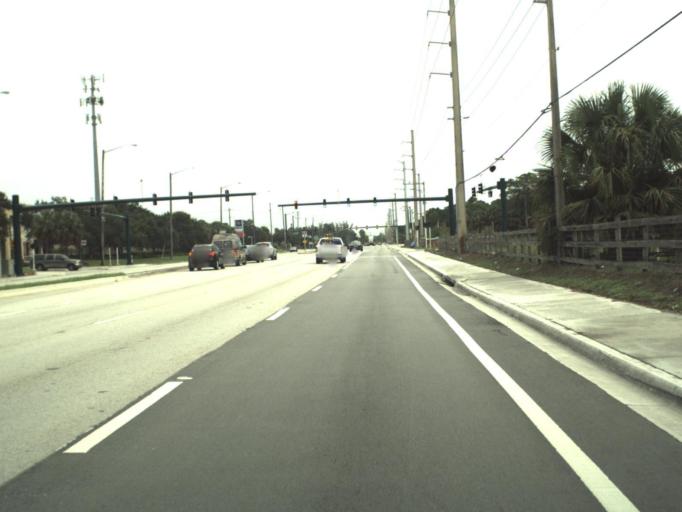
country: US
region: Florida
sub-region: Palm Beach County
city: Seminole Manor
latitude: 26.5734
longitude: -80.1132
